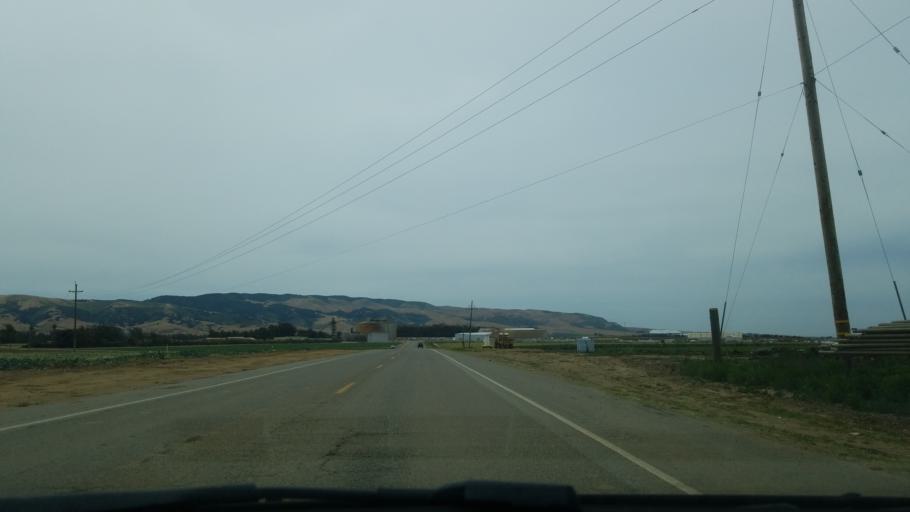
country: US
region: California
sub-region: Santa Barbara County
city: Santa Maria
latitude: 34.9197
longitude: -120.5046
